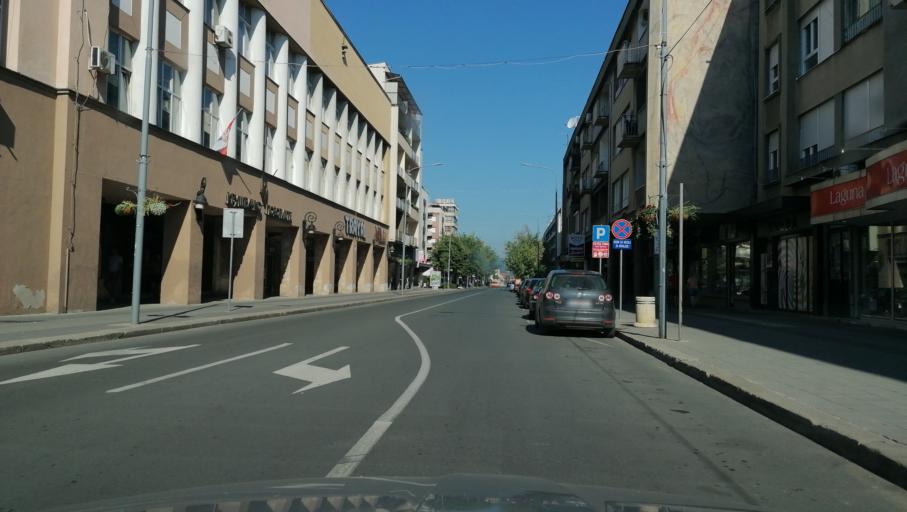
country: RS
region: Central Serbia
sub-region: Rasinski Okrug
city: Krusevac
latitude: 43.5808
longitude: 21.3296
